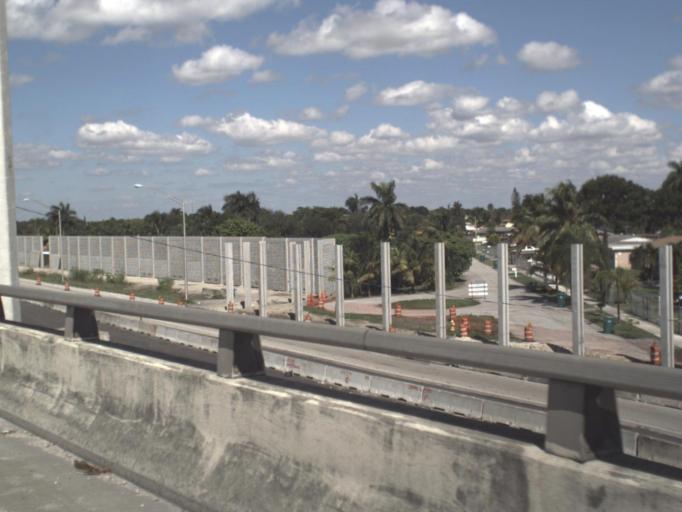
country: US
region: Florida
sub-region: Miami-Dade County
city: South Miami Heights
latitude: 25.5979
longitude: -80.3748
